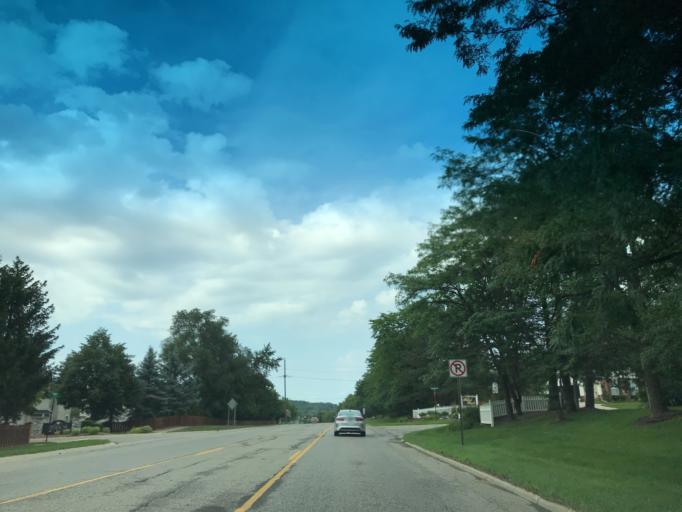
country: US
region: Michigan
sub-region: Oakland County
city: Milford
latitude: 42.5781
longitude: -83.6115
